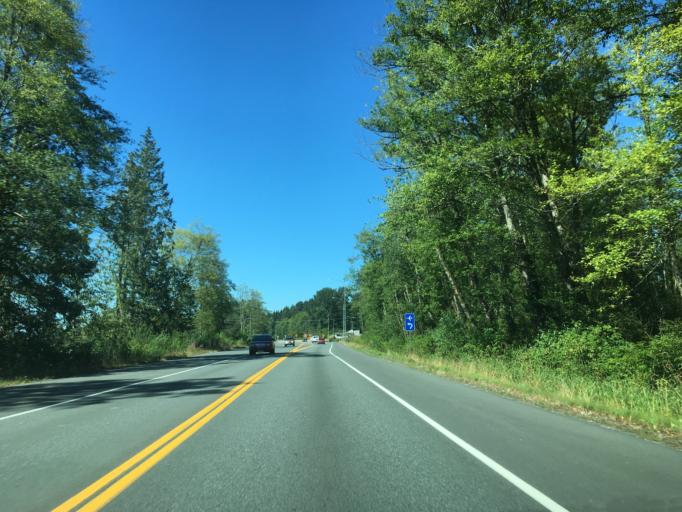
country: US
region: Washington
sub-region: Snohomish County
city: Sisco Heights
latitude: 48.1484
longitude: -122.1131
